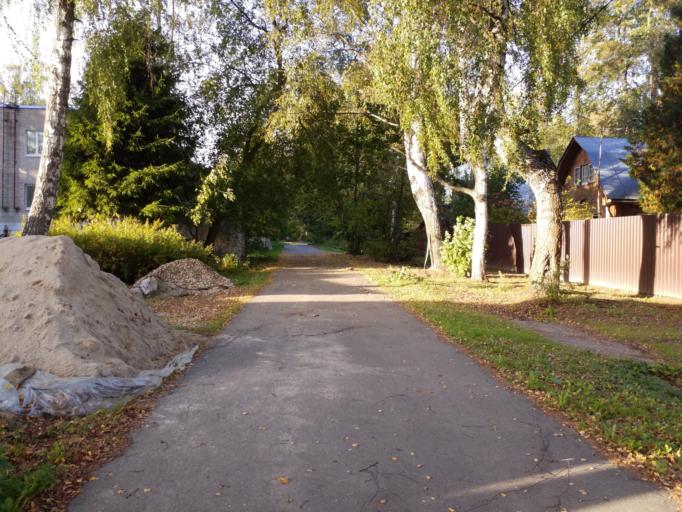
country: RU
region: Moskovskaya
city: Ashukino
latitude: 56.1642
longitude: 37.9556
